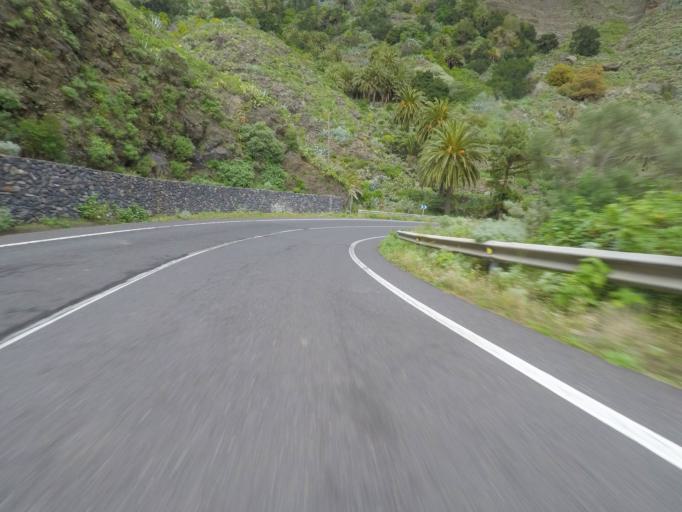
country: ES
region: Canary Islands
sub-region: Provincia de Santa Cruz de Tenerife
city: Hermigua
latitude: 28.1317
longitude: -17.1829
